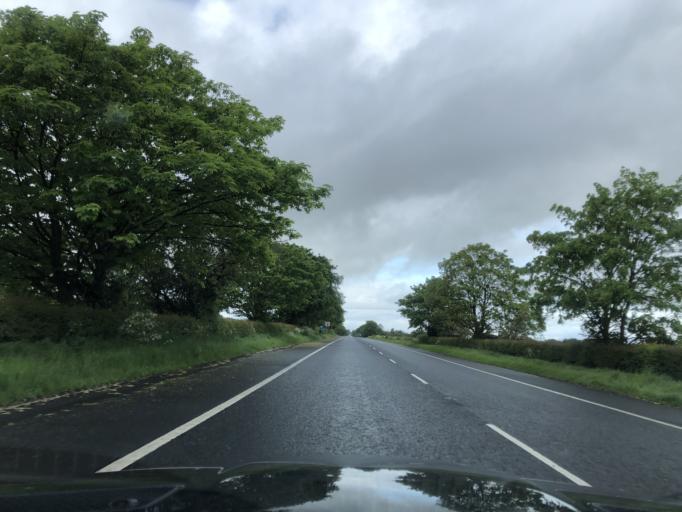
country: GB
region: Northern Ireland
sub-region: Ballymoney District
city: Ballymoney
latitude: 55.1027
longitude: -6.5391
